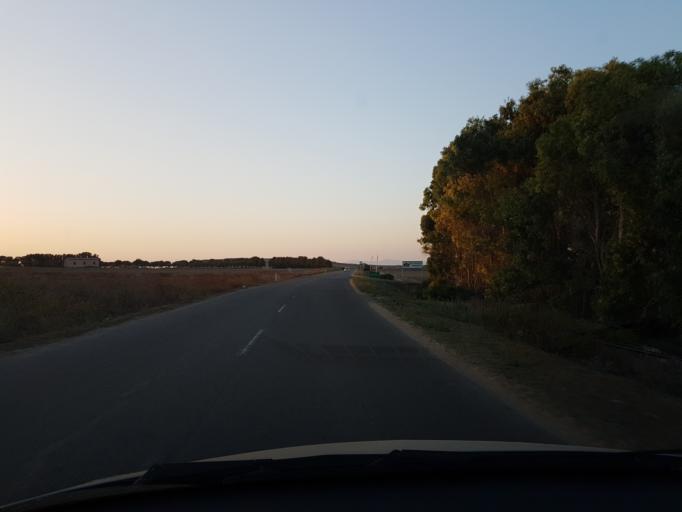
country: IT
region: Sardinia
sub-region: Provincia di Oristano
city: Nurachi
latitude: 39.9664
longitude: 8.4530
